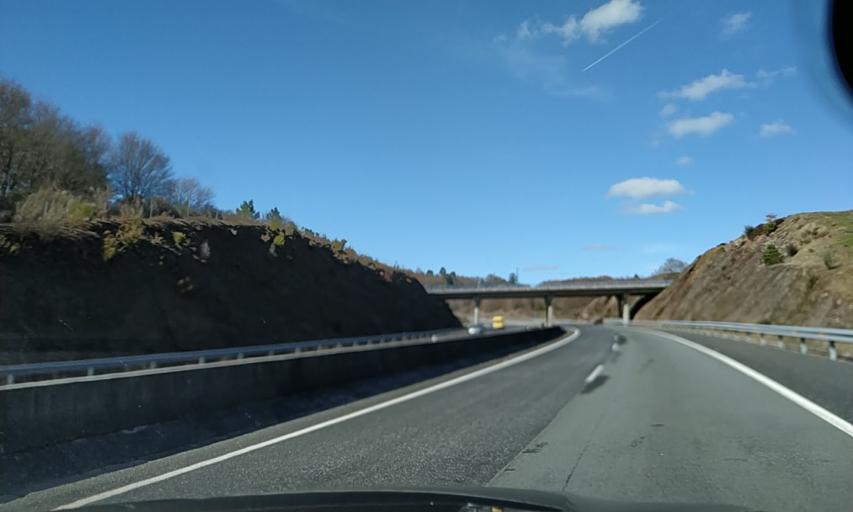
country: ES
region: Galicia
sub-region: Provincia de Pontevedra
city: Lalin
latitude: 42.6195
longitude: -8.0982
